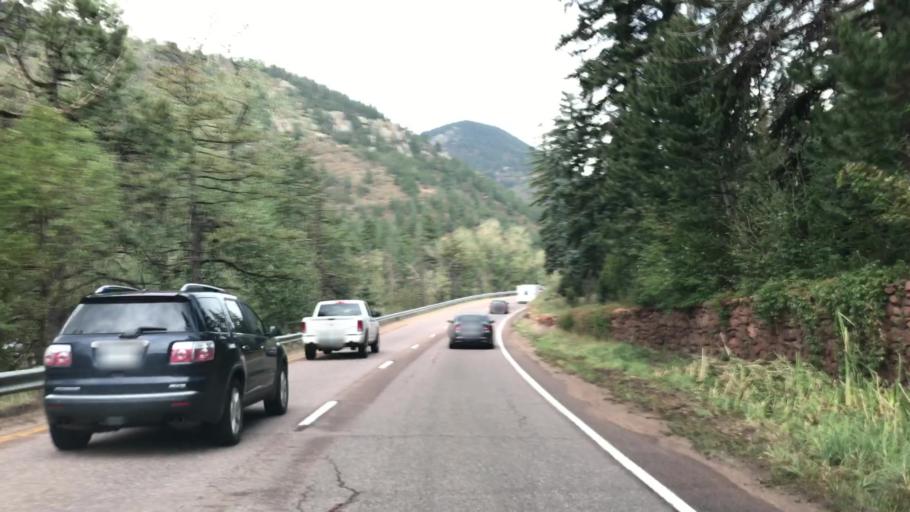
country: US
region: Colorado
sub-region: El Paso County
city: Manitou Springs
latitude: 38.8890
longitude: -104.9636
